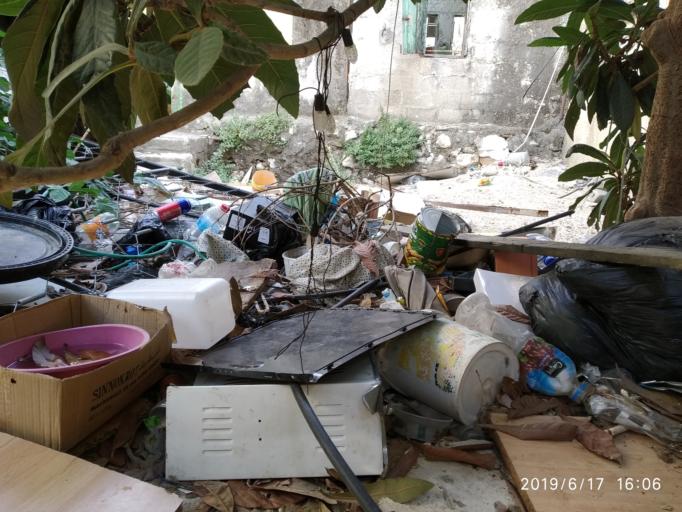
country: PS
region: West Bank
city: Iktabah
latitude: 32.3187
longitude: 35.0563
